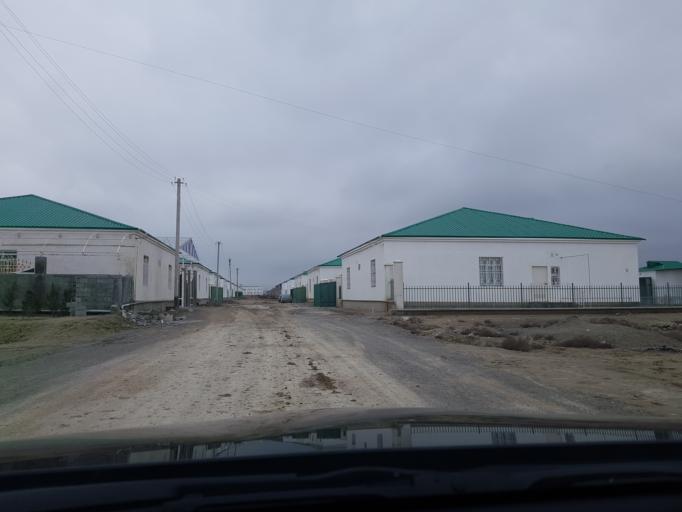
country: TM
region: Ahal
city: Abadan
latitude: 38.1574
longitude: 57.9499
